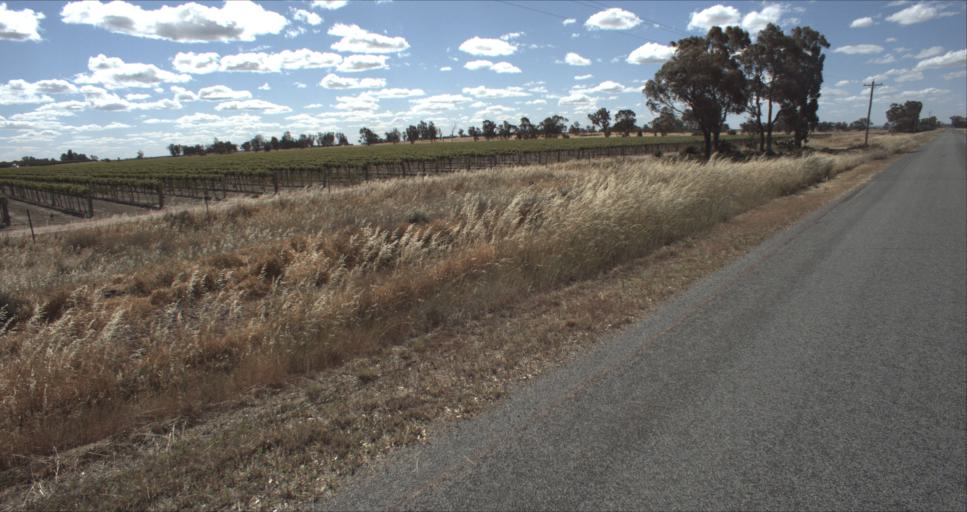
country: AU
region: New South Wales
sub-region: Leeton
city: Leeton
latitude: -34.4943
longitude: 146.2467
